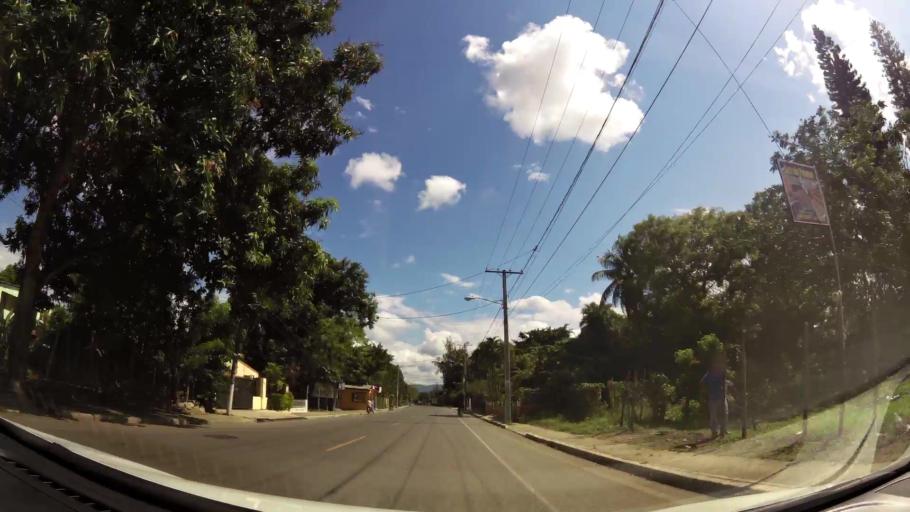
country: DO
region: La Vega
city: Concepcion de La Vega
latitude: 19.2426
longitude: -70.5369
